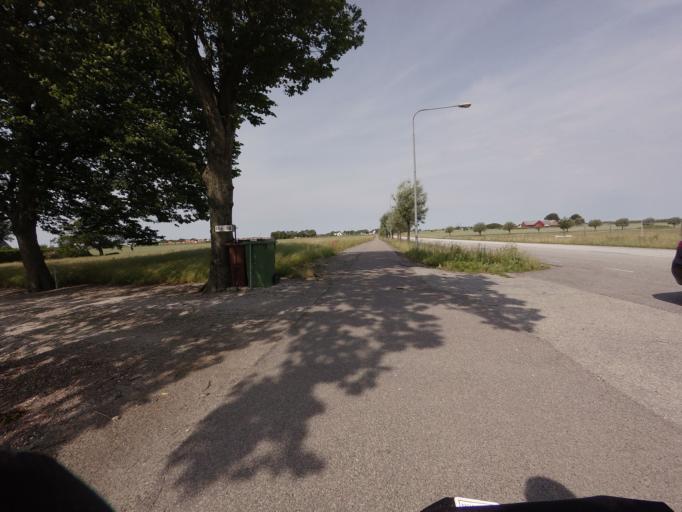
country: SE
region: Skane
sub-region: Malmo
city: Bunkeflostrand
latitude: 55.5286
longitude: 12.9533
